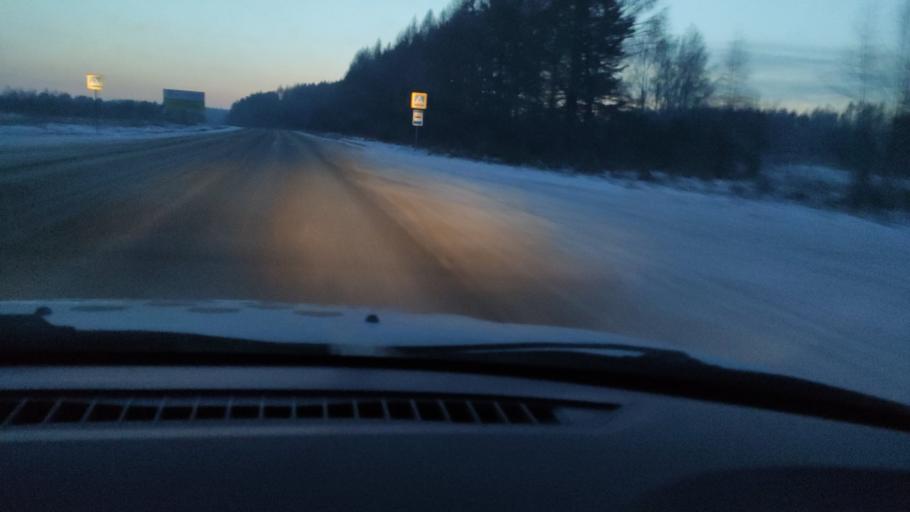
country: RU
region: Perm
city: Kungur
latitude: 57.4202
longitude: 56.9205
